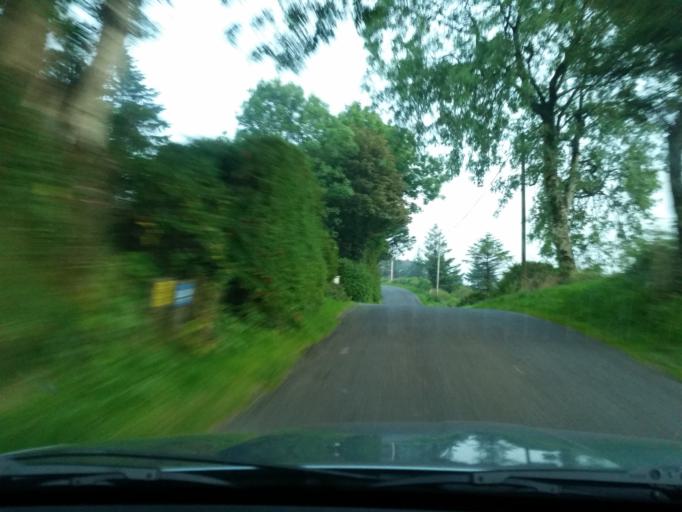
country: GB
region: Northern Ireland
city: Fivemiletown
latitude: 54.2800
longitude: -7.2773
